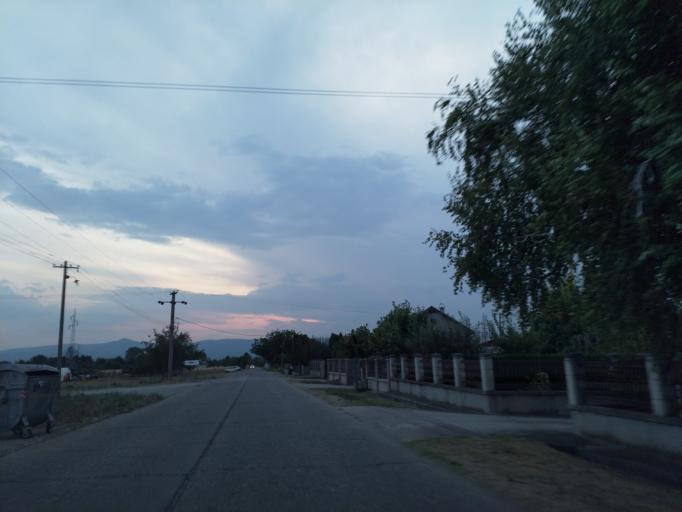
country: RS
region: Central Serbia
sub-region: Pomoravski Okrug
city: Paracin
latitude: 43.8660
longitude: 21.4439
